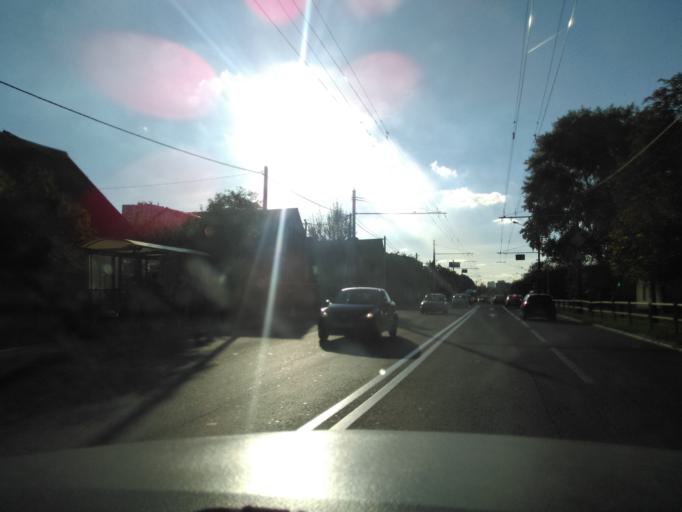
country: BY
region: Minsk
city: Minsk
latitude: 53.9071
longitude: 27.6248
